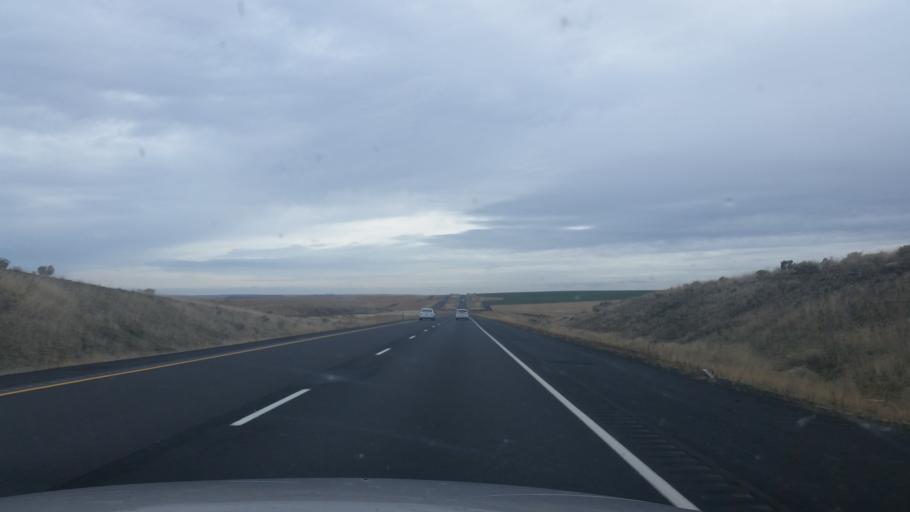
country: US
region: Washington
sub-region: Grant County
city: Warden
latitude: 47.0865
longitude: -118.7395
